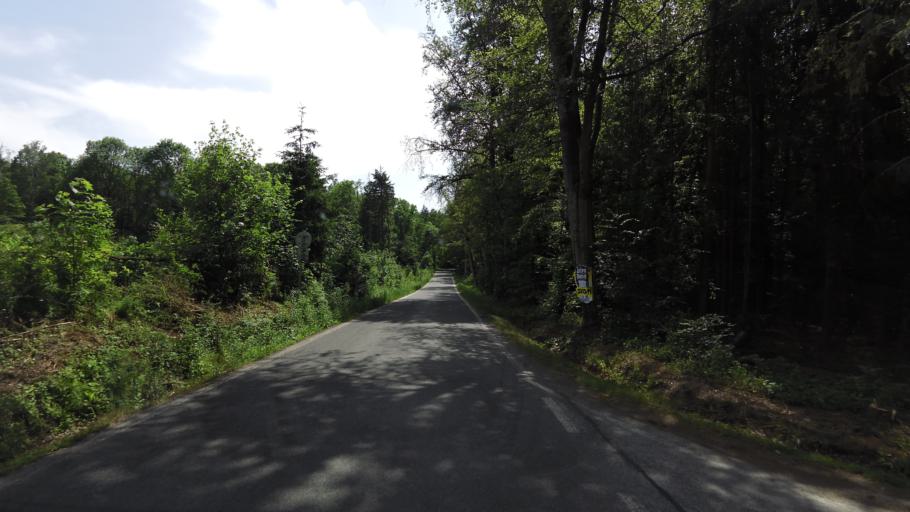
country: CZ
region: Plzensky
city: Stary Plzenec
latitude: 49.6493
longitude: 13.4530
